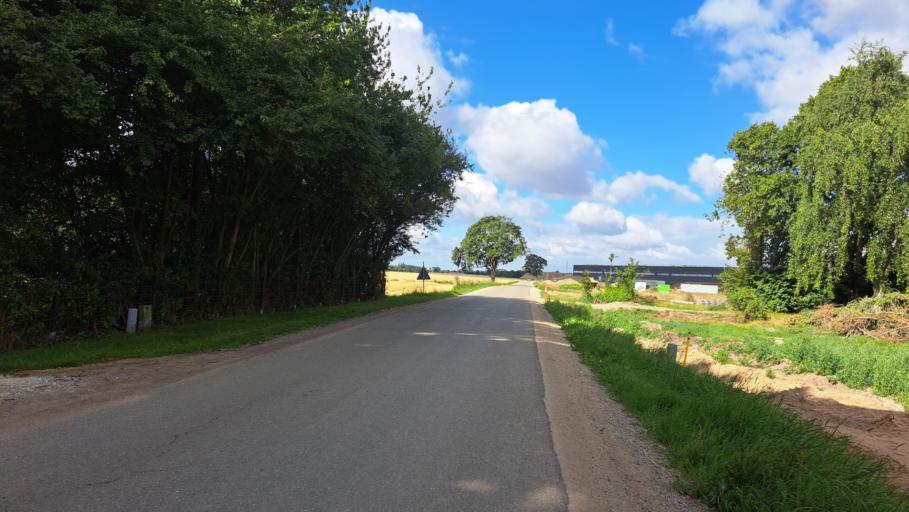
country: DK
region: Central Jutland
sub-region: Hedensted Kommune
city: Hedensted
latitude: 55.7764
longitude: 9.6664
